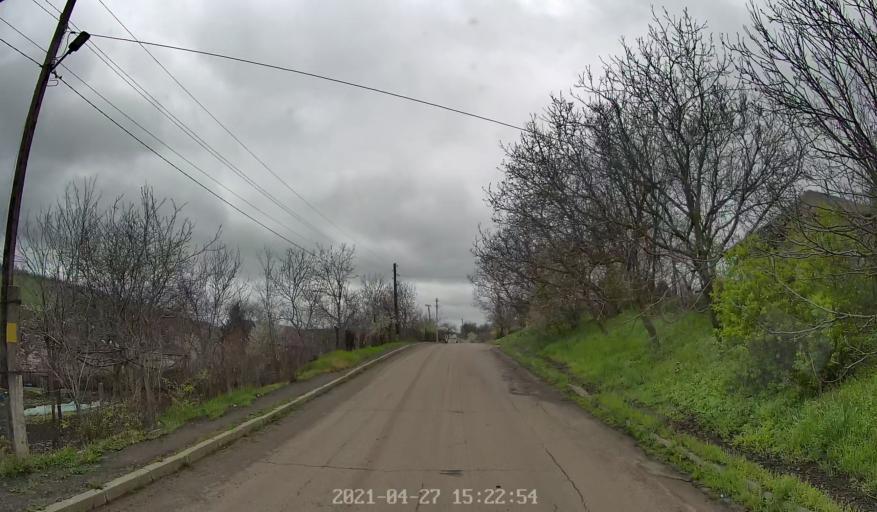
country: MD
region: Chisinau
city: Vadul lui Voda
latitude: 47.0259
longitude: 29.0248
